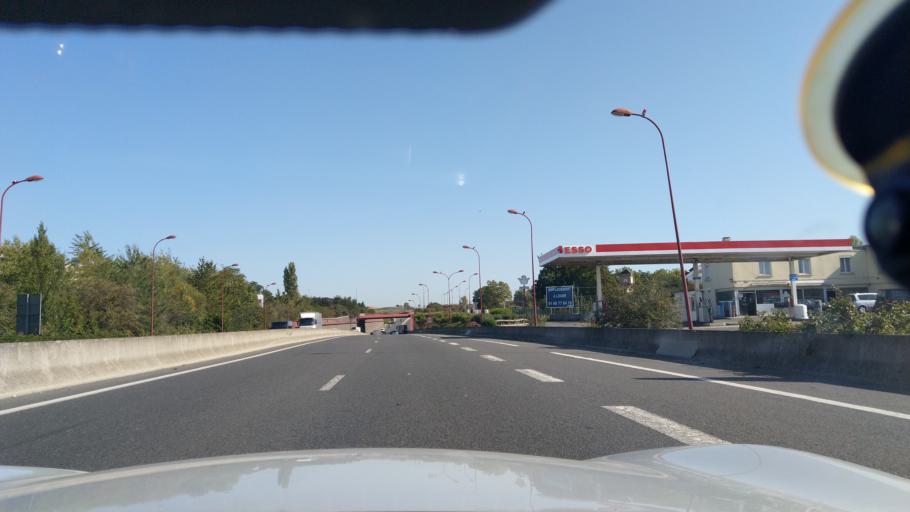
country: FR
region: Ile-de-France
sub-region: Departement du Val-d'Oise
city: Gonesse
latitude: 48.9809
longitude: 2.4673
